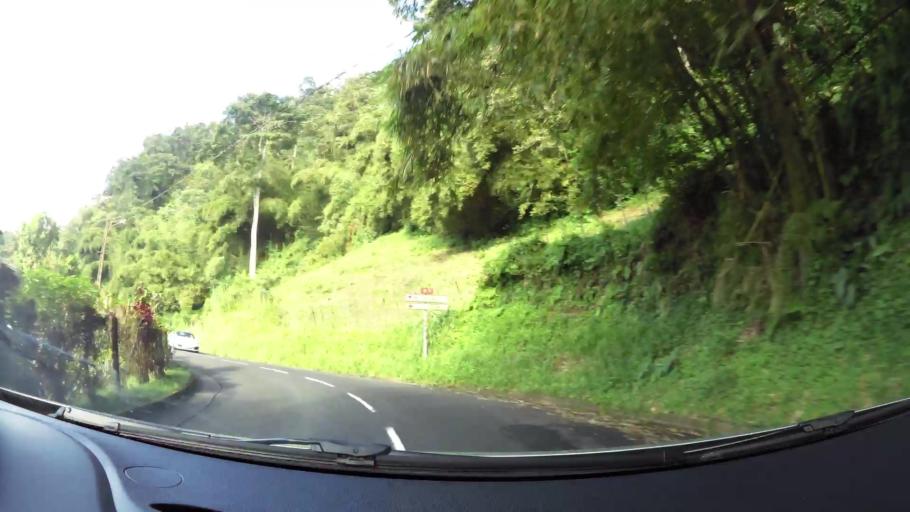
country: MQ
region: Martinique
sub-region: Martinique
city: Saint-Joseph
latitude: 14.6736
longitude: -61.0907
